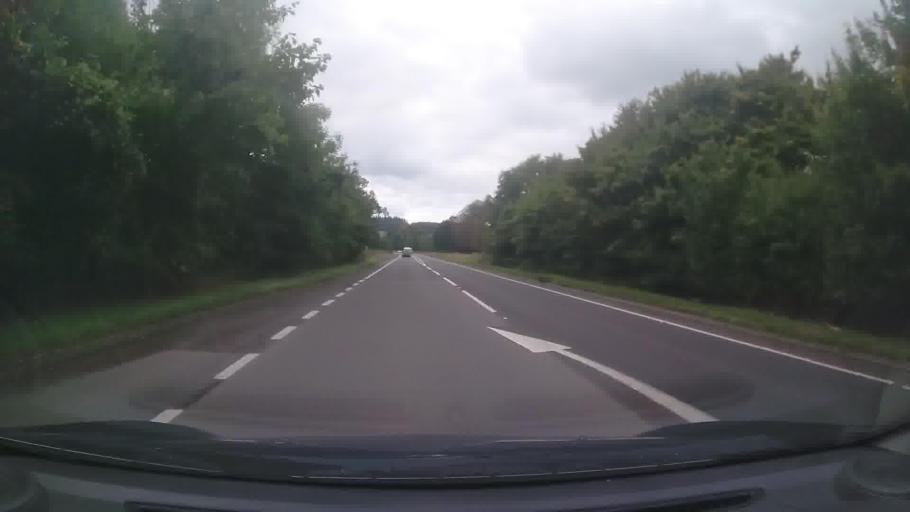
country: GB
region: England
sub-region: Shropshire
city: Oswestry
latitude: 52.8357
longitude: -3.0500
